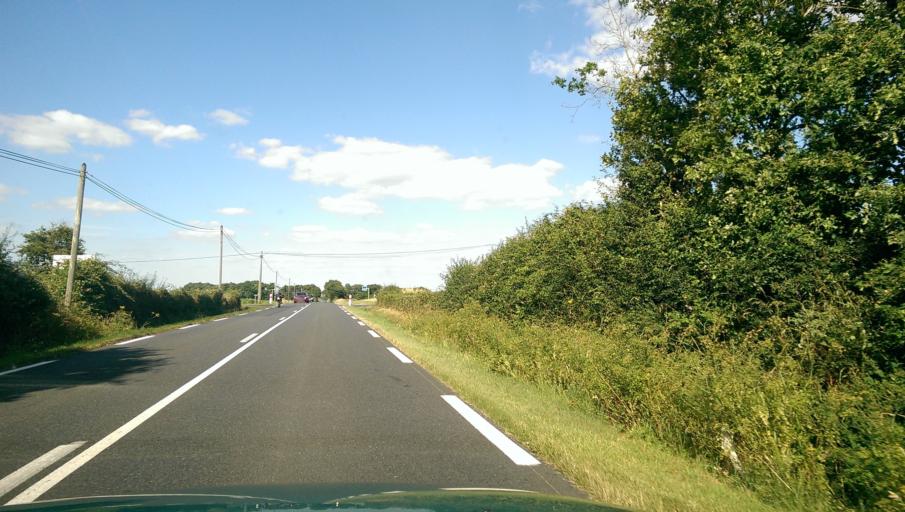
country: FR
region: Pays de la Loire
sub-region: Departement de la Vendee
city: Rocheserviere
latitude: 46.9508
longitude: -1.4800
